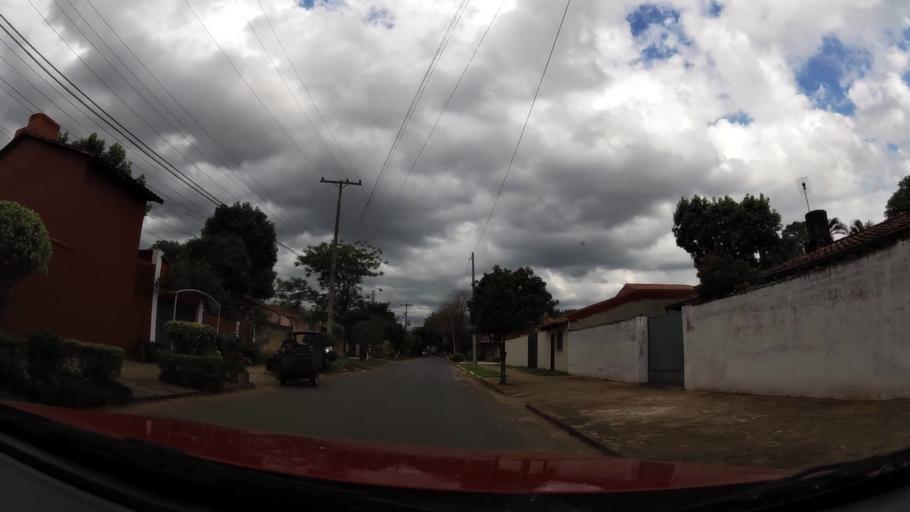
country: PY
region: Central
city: San Lorenzo
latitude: -25.2780
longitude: -57.4928
